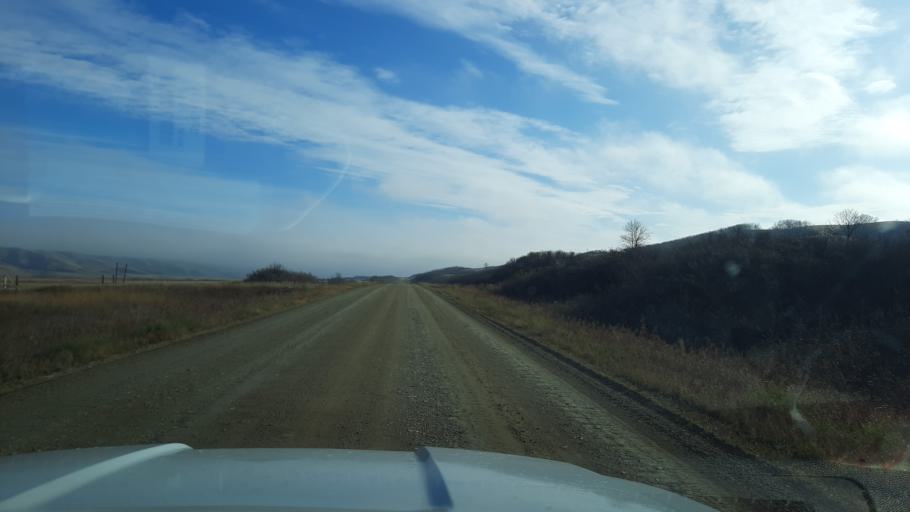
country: CA
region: Saskatchewan
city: Pilot Butte
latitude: 50.7836
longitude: -104.2474
